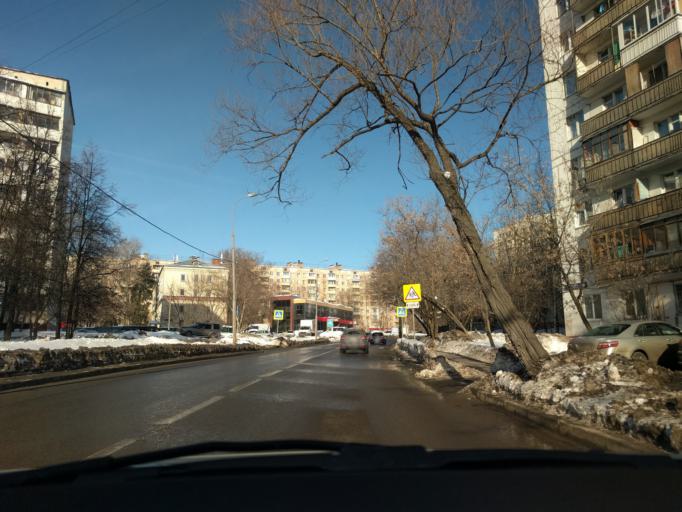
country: RU
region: Moskovskaya
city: Izmaylovo
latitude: 55.7990
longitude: 37.8242
